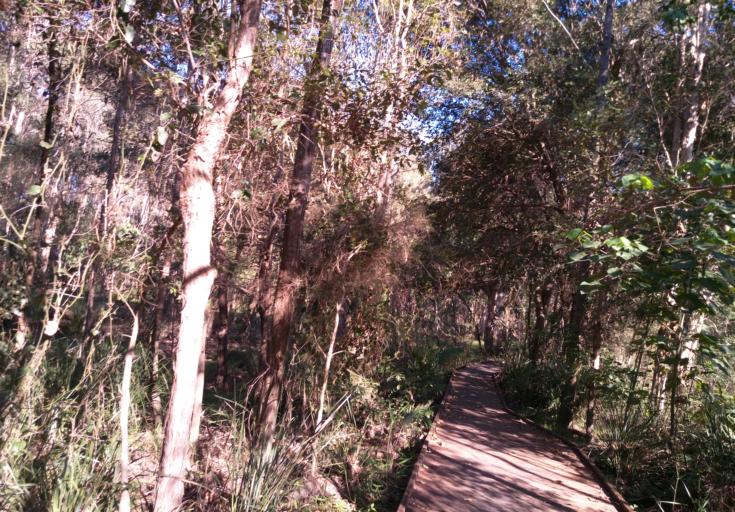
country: AU
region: Queensland
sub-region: Brisbane
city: Chandler
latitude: -27.5219
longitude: 153.1975
